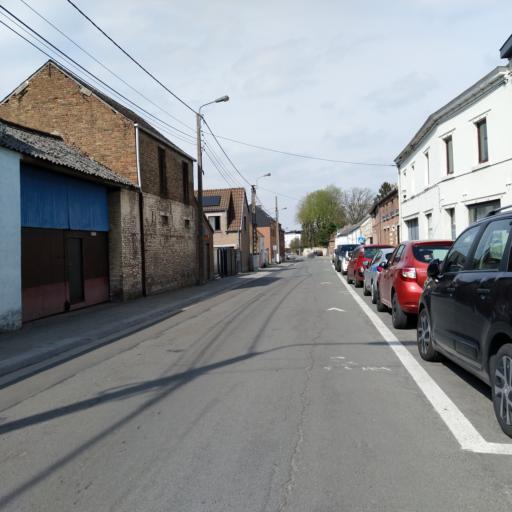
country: BE
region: Wallonia
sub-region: Province du Hainaut
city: Mons
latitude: 50.4408
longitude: 3.9626
